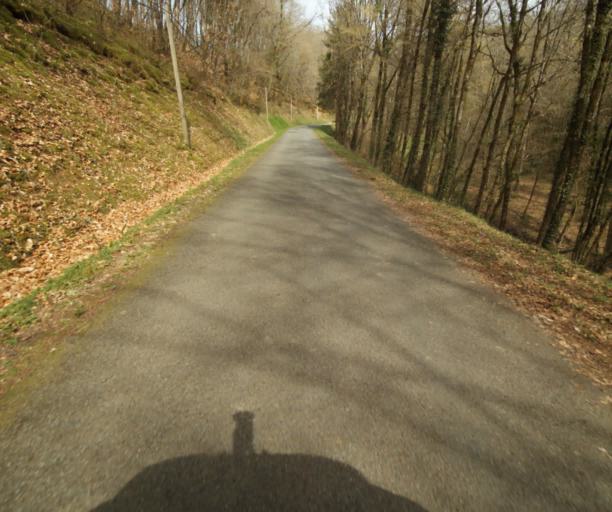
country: FR
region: Limousin
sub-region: Departement de la Correze
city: Naves
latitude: 45.3526
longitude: 1.8142
